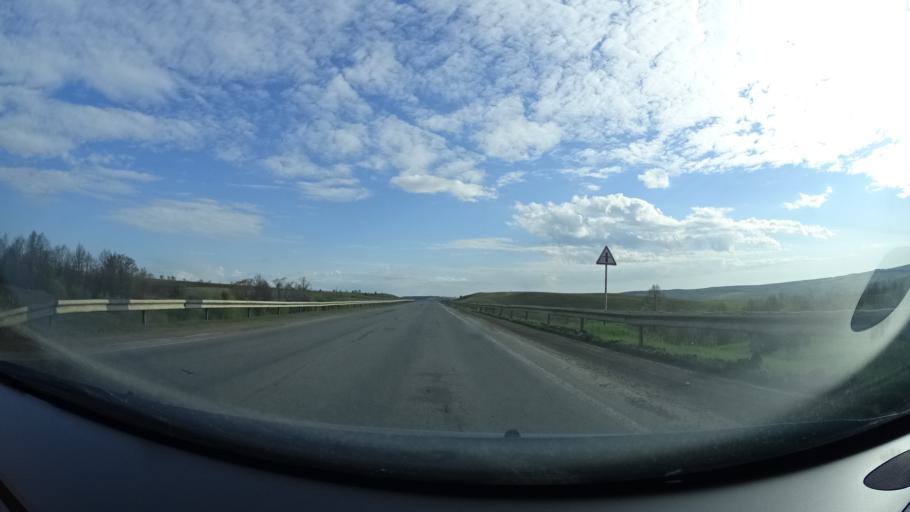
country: RU
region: Bashkortostan
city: Blagoveshchensk
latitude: 55.0935
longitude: 55.8145
